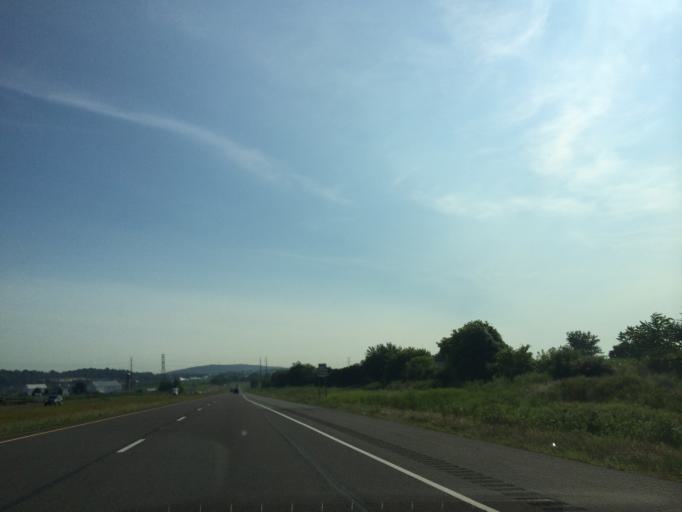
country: US
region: Pennsylvania
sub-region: Lancaster County
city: Brownstown
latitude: 40.1341
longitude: -76.2112
